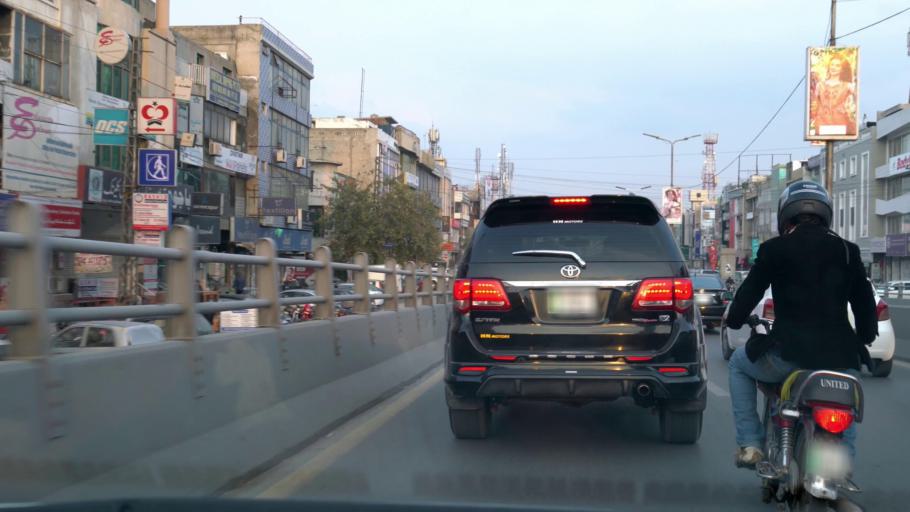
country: PK
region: Punjab
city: Lahore
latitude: 31.5020
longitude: 74.3590
